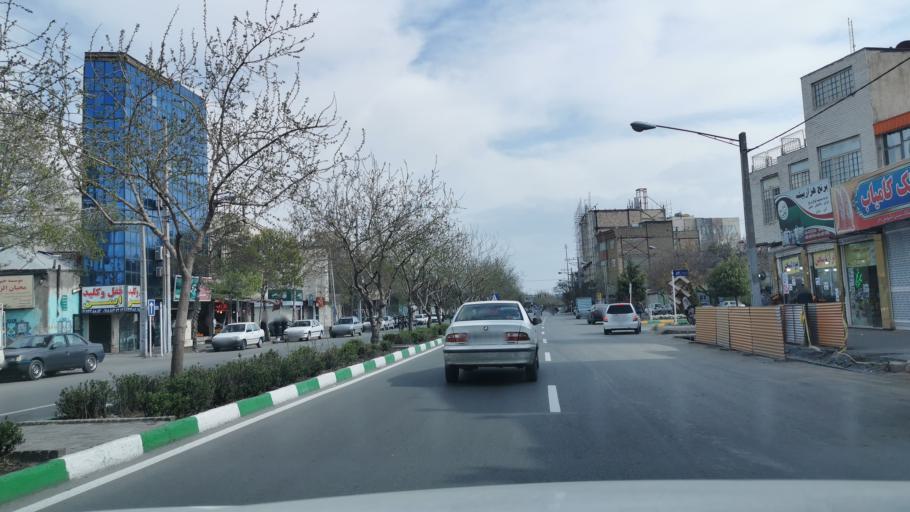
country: IR
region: Razavi Khorasan
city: Mashhad
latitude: 36.3134
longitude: 59.6124
